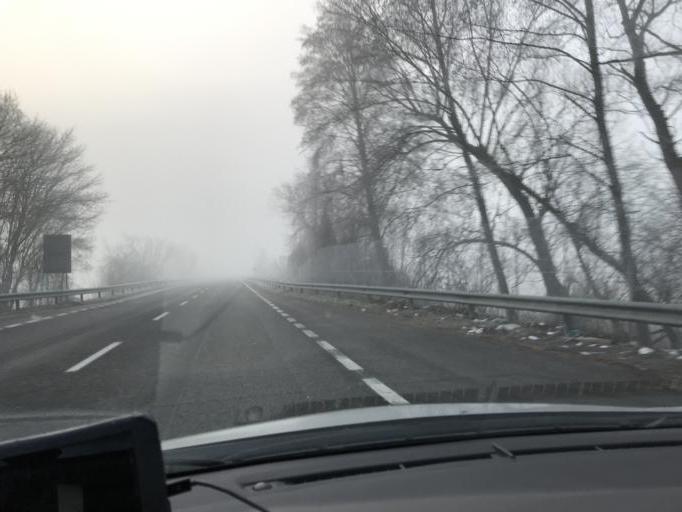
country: IT
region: Latium
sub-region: Provincia di Rieti
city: Colli sul Velino
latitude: 42.4826
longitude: 12.7694
